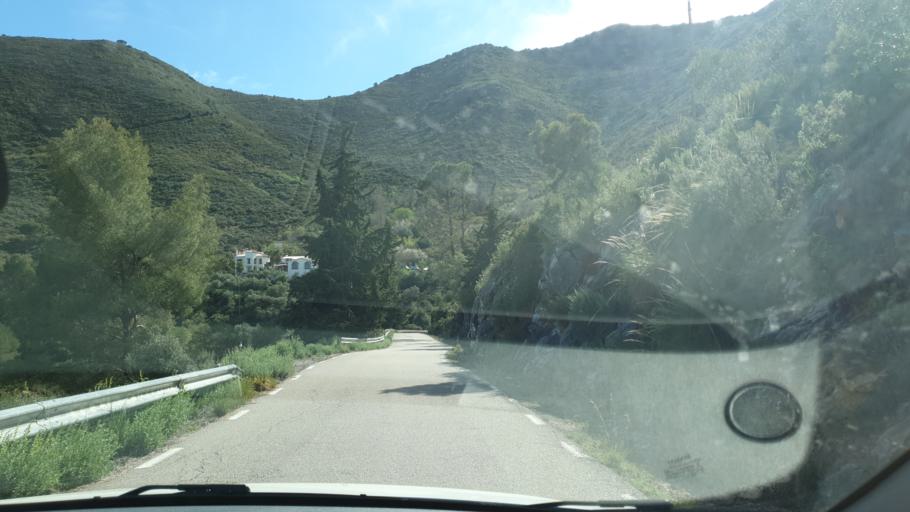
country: ES
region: Andalusia
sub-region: Provincia de Malaga
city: Ojen
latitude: 36.5885
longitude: -4.8720
